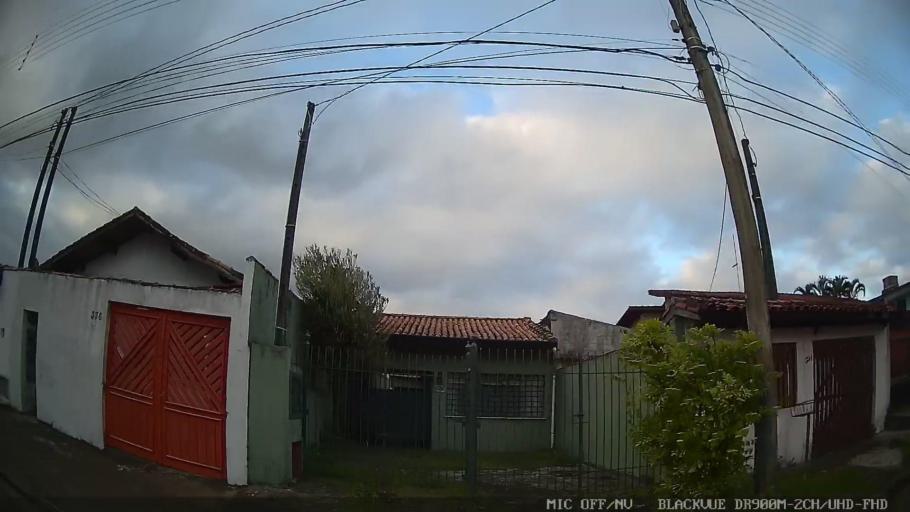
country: BR
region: Sao Paulo
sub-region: Peruibe
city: Peruibe
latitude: -24.3097
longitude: -46.9923
